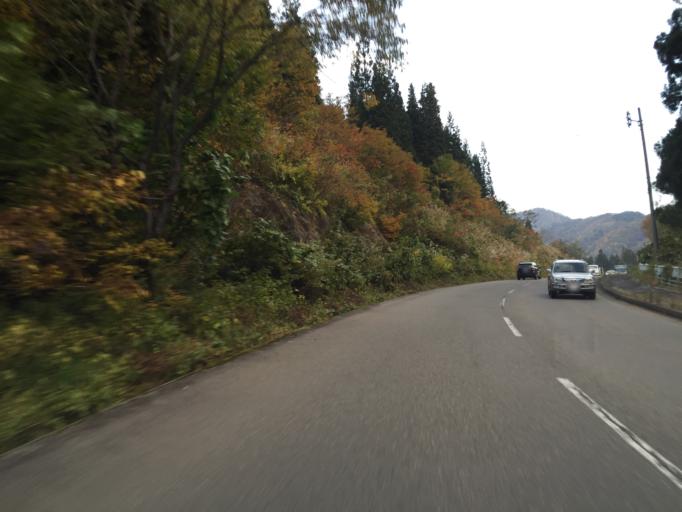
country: JP
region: Yamagata
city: Yonezawa
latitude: 37.8386
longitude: 140.0004
